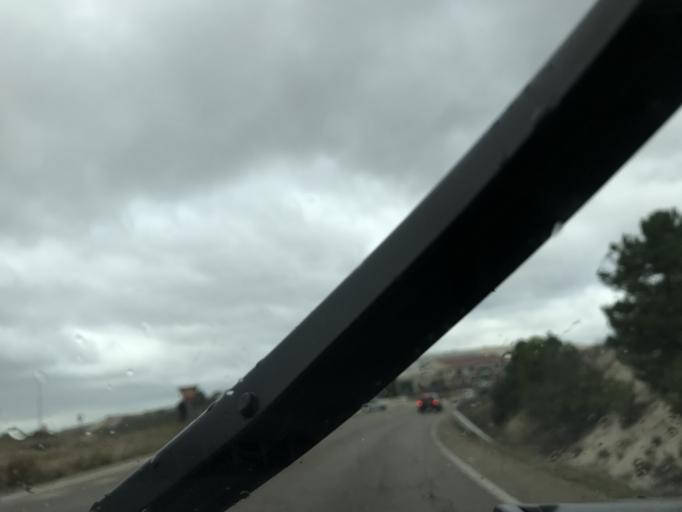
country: ES
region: Andalusia
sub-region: Provincia de Jaen
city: Peal de Becerro
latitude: 37.9181
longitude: -3.1307
